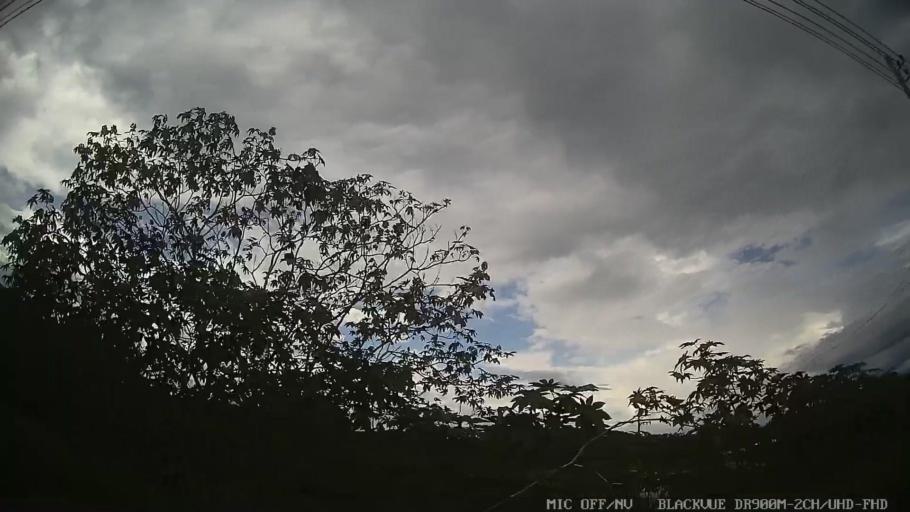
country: BR
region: Sao Paulo
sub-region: Biritiba-Mirim
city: Biritiba Mirim
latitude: -23.5668
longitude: -46.0466
